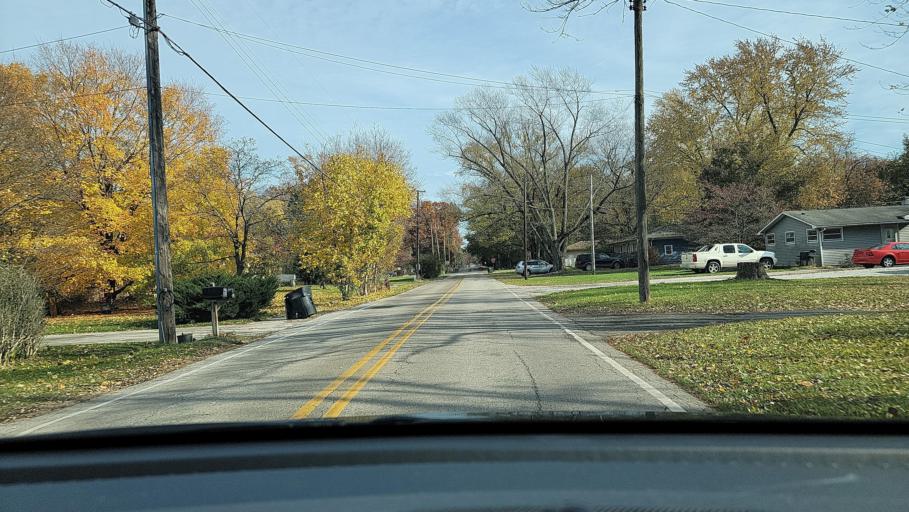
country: US
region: Indiana
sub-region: Porter County
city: Portage
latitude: 41.5795
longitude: -87.1994
